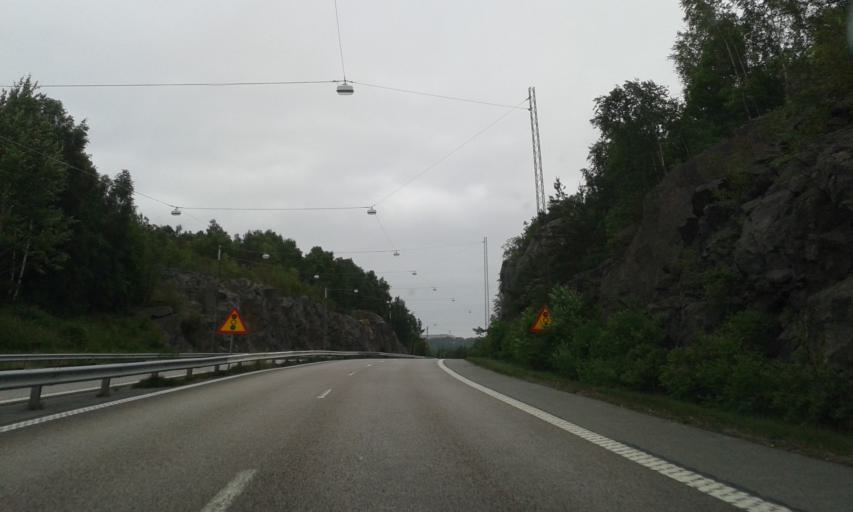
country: SE
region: Vaestra Goetaland
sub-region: Goteborg
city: Hammarkullen
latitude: 57.7878
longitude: 12.0360
